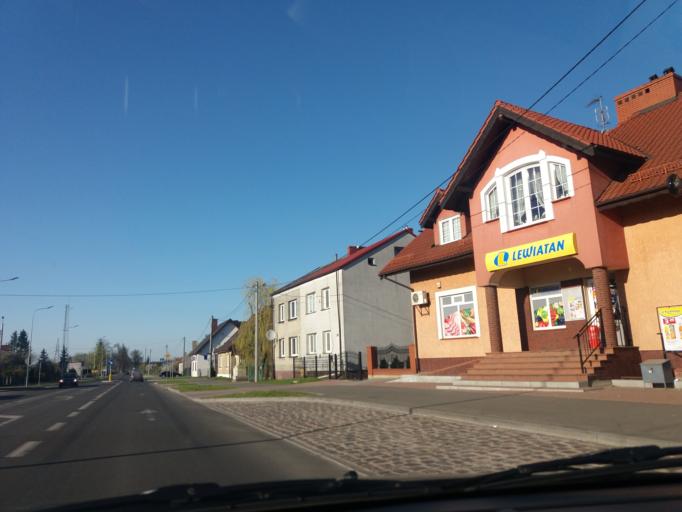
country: PL
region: Warmian-Masurian Voivodeship
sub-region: Powiat nidzicki
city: Nidzica
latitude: 53.3722
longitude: 20.4289
